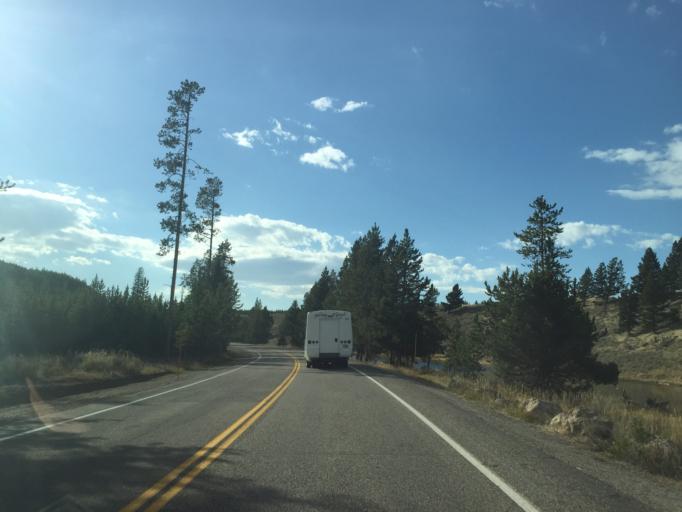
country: US
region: Montana
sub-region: Gallatin County
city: West Yellowstone
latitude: 44.6691
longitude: -110.9762
